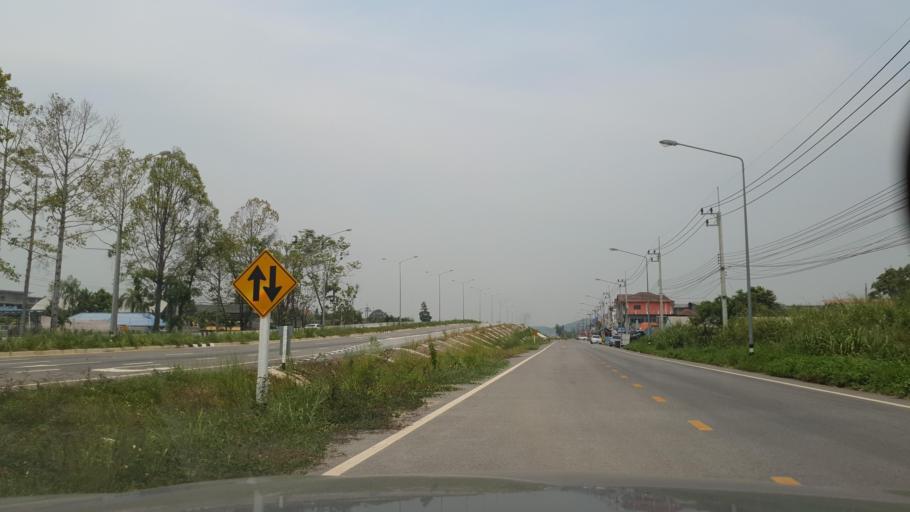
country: TH
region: Rayong
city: Ban Chang
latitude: 12.7125
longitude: 101.0035
